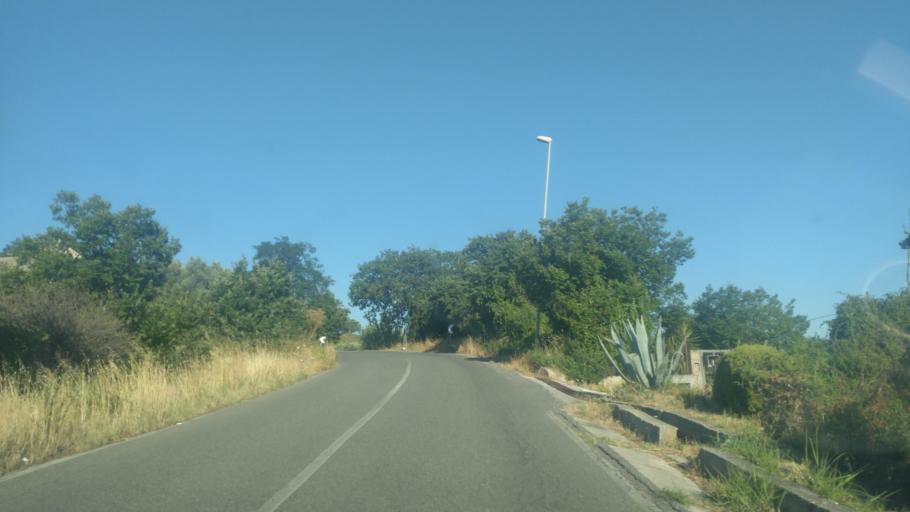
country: IT
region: Calabria
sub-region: Provincia di Catanzaro
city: Staletti
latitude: 38.7676
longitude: 16.5245
